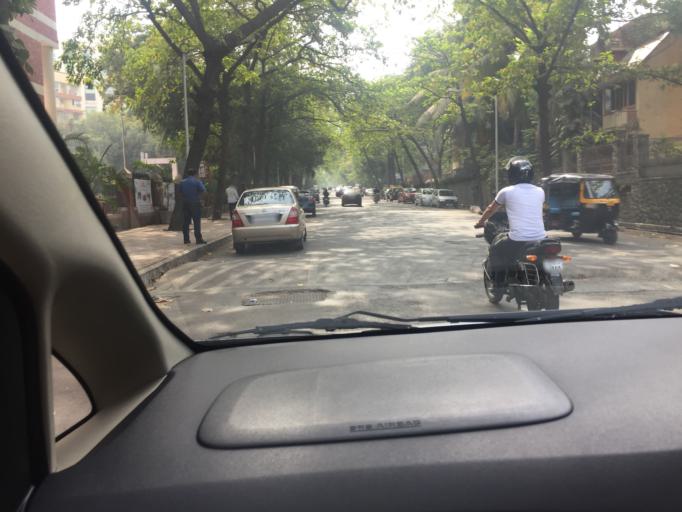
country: IN
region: Maharashtra
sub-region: Mumbai Suburban
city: Powai
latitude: 19.1179
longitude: 72.9074
